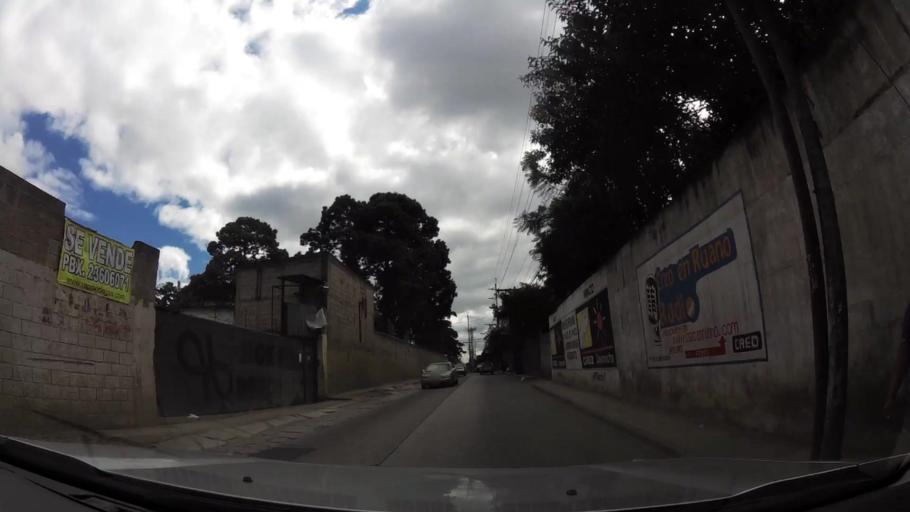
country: GT
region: Guatemala
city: Mixco
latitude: 14.6383
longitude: -90.5996
